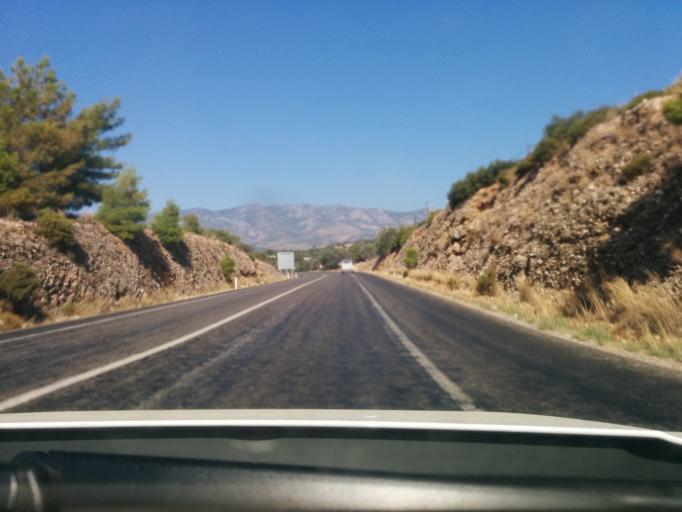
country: TR
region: Mugla
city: Esen
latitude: 36.4069
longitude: 29.2840
